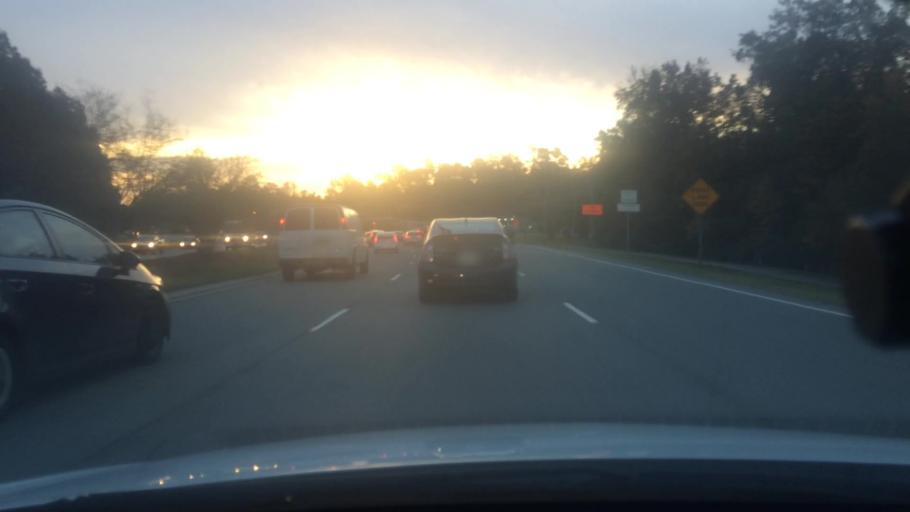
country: US
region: North Carolina
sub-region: Orange County
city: Chapel Hill
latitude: 35.9018
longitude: -79.0098
